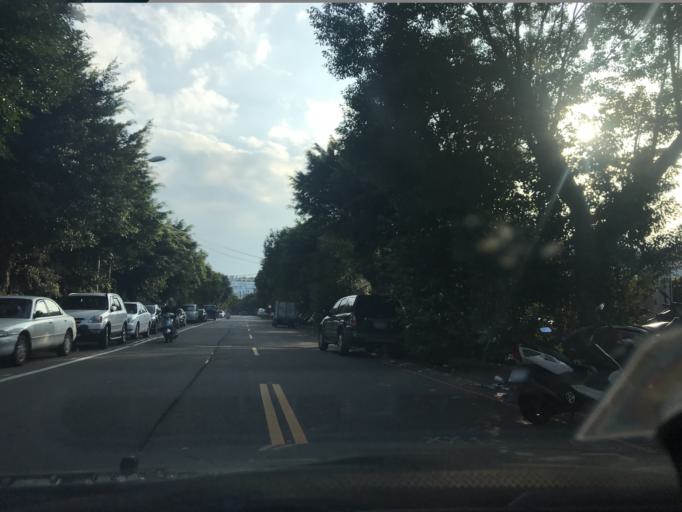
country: TW
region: Taiwan
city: Taoyuan City
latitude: 24.9847
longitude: 121.2360
